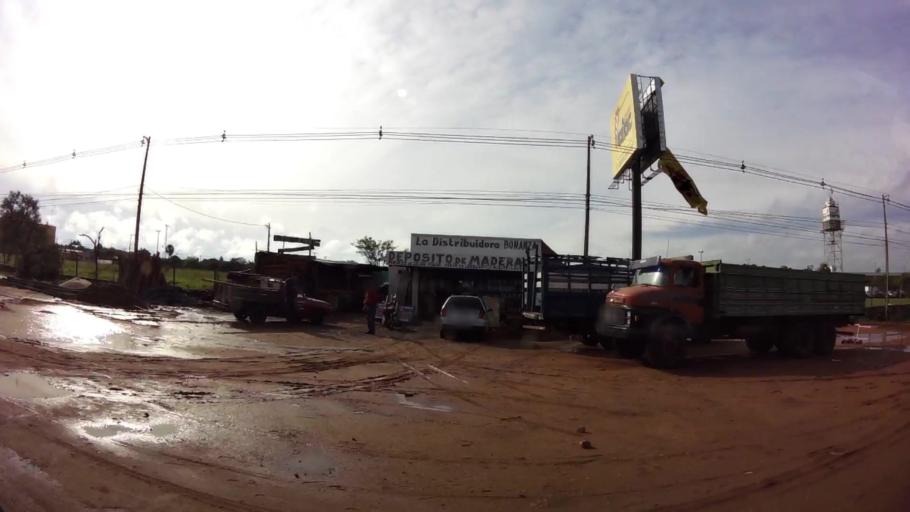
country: PY
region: Central
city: Limpio
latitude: -25.1755
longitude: -57.4843
